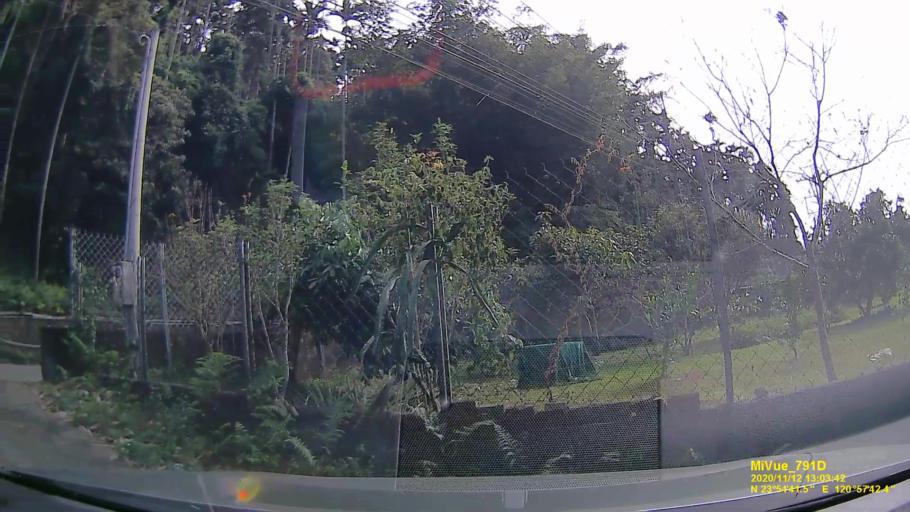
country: TW
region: Taiwan
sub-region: Nantou
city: Puli
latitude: 23.9115
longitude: 120.9618
